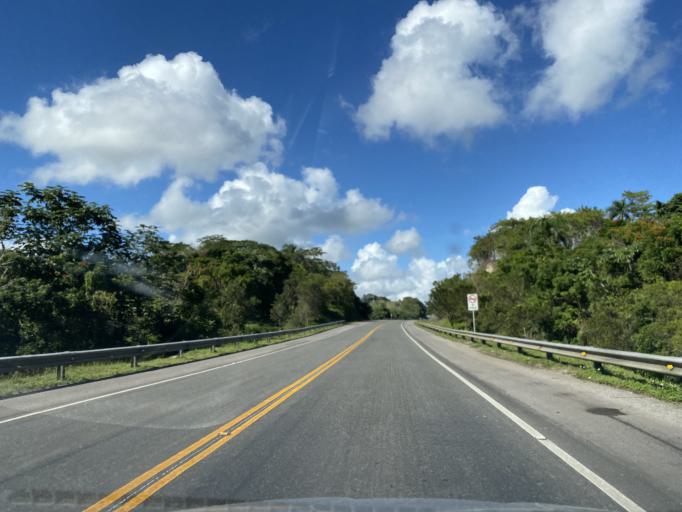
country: DO
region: Monte Plata
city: Majagual
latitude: 19.0310
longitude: -69.8255
